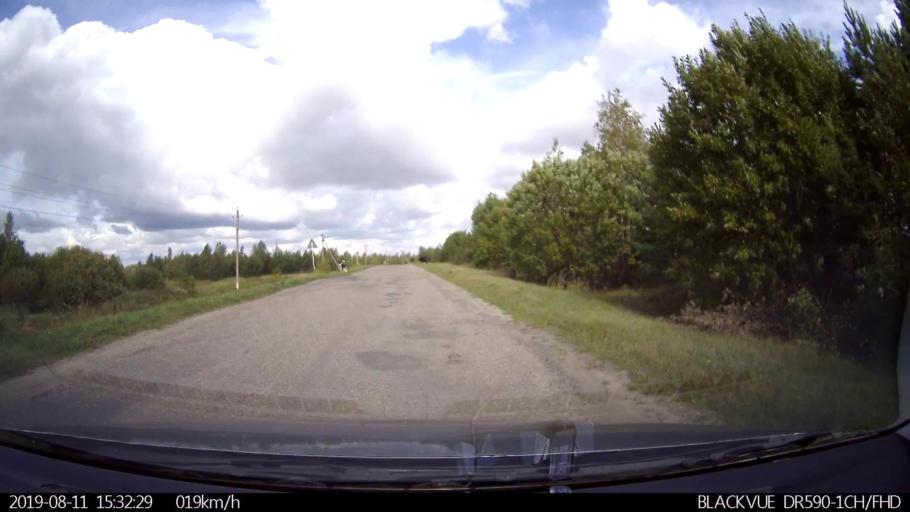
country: RU
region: Ulyanovsk
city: Ignatovka
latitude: 53.8604
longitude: 47.5759
